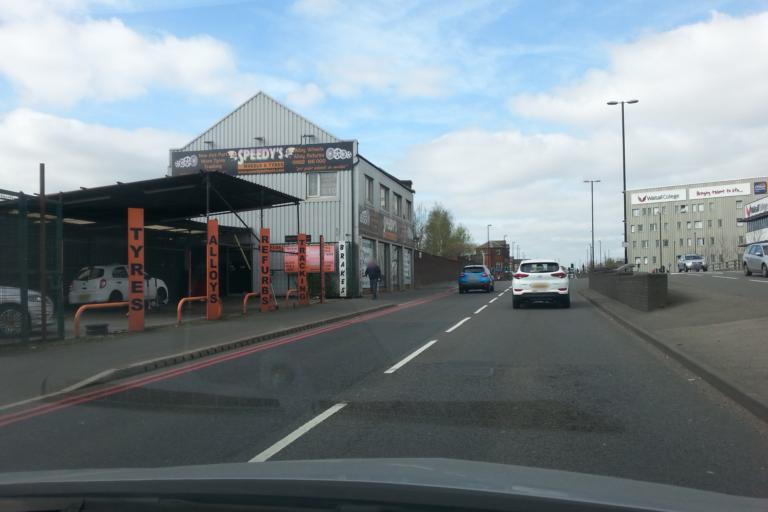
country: GB
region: England
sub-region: Walsall
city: Walsall
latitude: 52.5887
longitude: -1.9799
